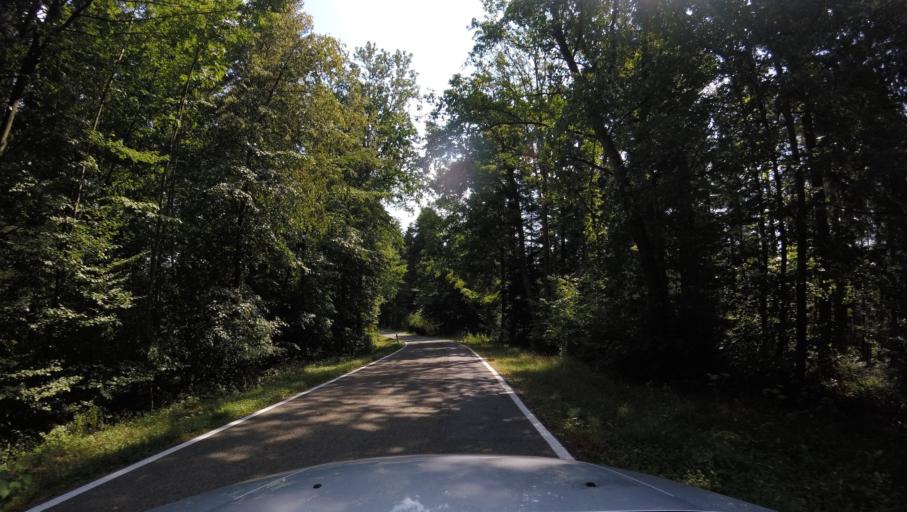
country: DE
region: Baden-Wuerttemberg
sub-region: Regierungsbezirk Stuttgart
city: Alfdorf
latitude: 48.8767
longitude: 9.6920
